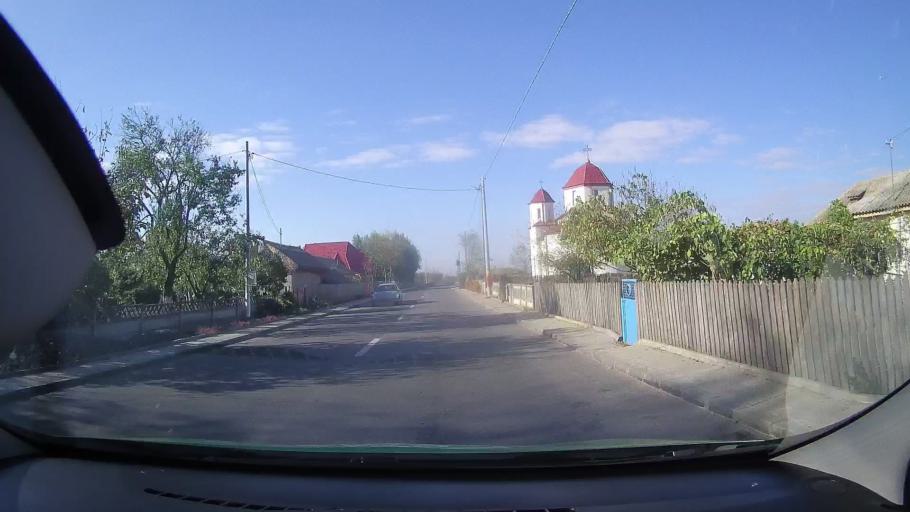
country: RO
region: Tulcea
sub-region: Comuna Murighiol
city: Murighiol
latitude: 45.0202
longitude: 29.1192
